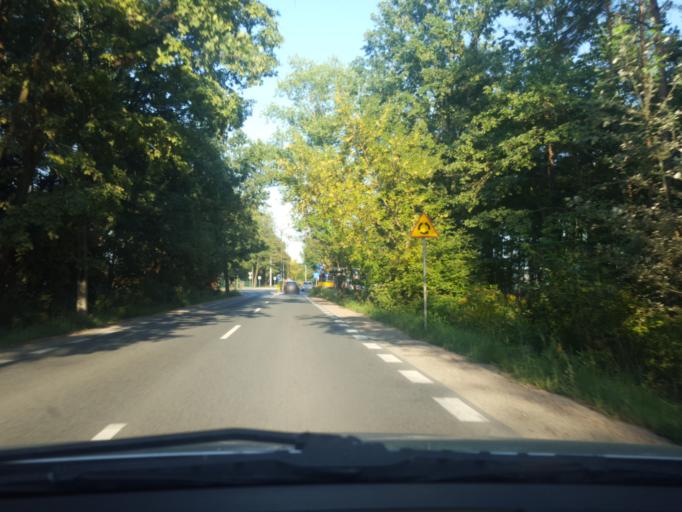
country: PL
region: Masovian Voivodeship
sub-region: Warszawa
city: Rembertow
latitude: 52.2606
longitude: 21.1495
